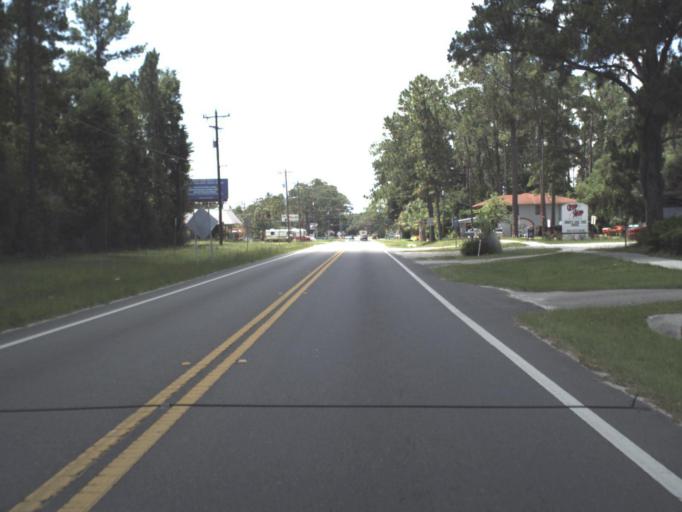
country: US
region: Florida
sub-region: Clay County
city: Keystone Heights
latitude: 29.7134
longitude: -82.0445
